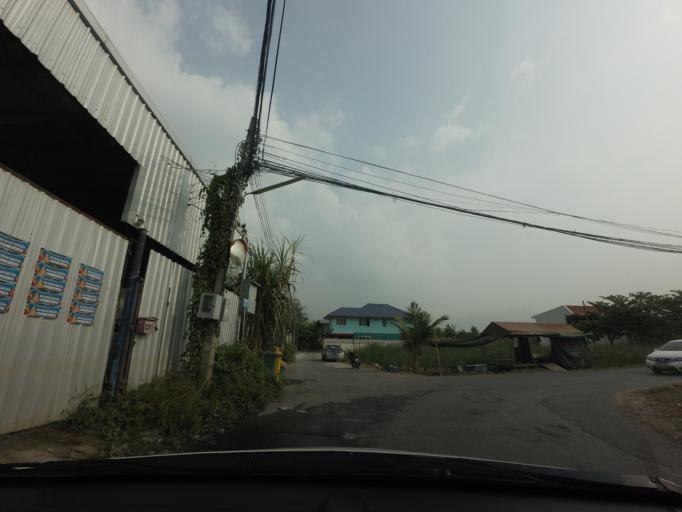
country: TH
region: Bangkok
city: Nong Khaem
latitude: 13.7343
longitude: 100.3376
